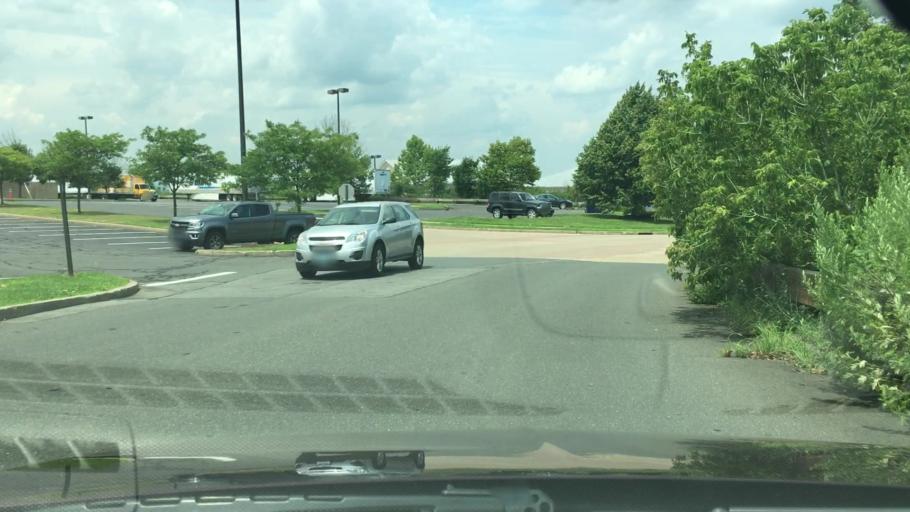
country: US
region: Connecticut
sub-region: Hartford County
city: Manchester
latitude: 41.8094
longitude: -72.5526
